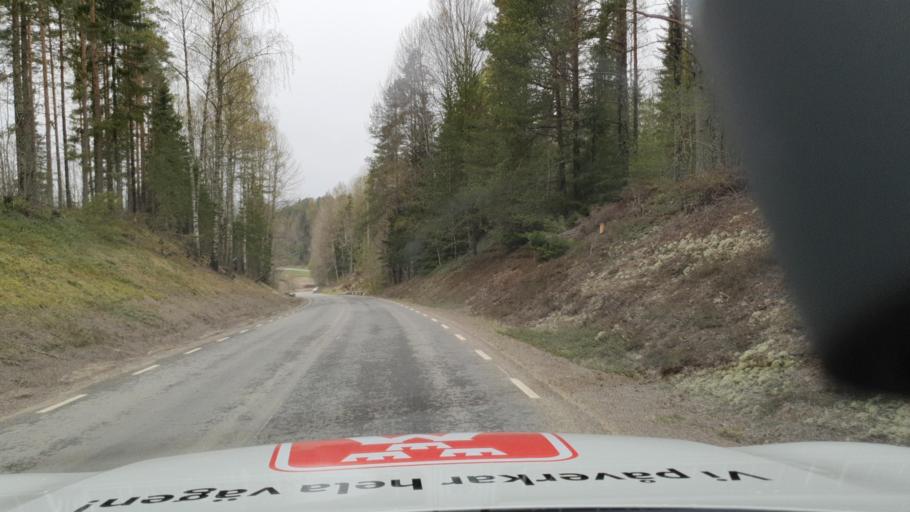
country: SE
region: Vaesterbotten
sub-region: Nordmalings Kommun
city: Nordmaling
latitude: 63.7220
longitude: 19.5369
